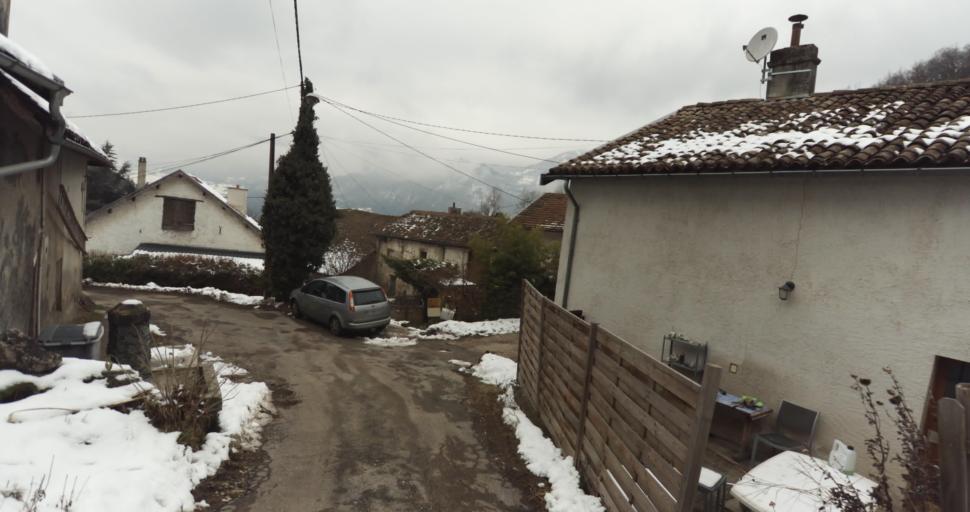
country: FR
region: Rhone-Alpes
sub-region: Departement de l'Isere
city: Vif
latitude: 45.0194
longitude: 5.6702
